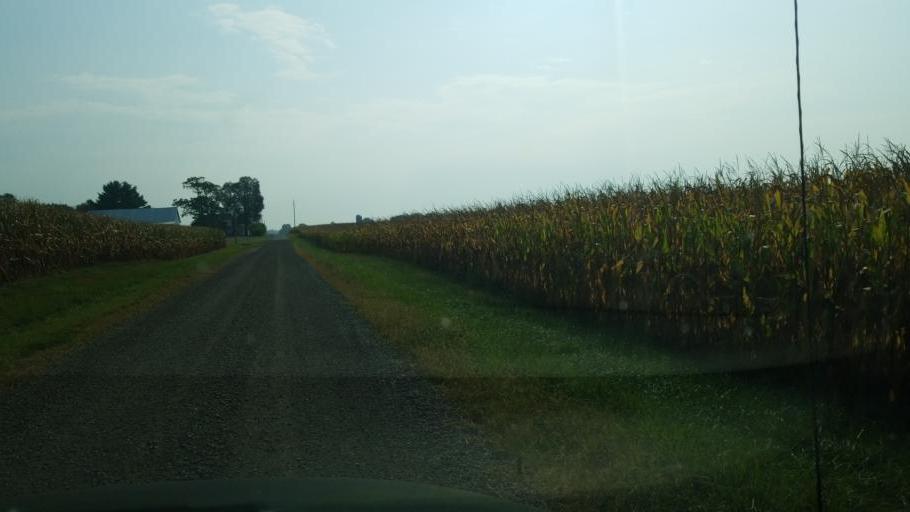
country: US
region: Ohio
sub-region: Knox County
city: Centerburg
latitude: 40.2939
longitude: -82.5922
